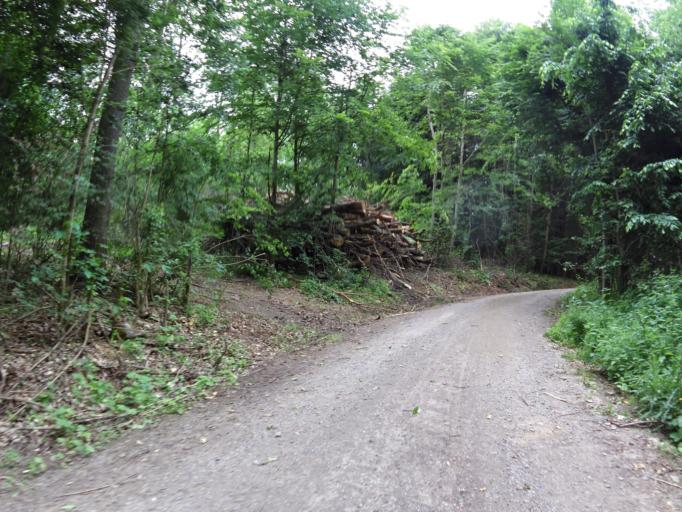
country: DE
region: Bavaria
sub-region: Regierungsbezirk Unterfranken
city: Hettstadt
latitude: 49.8160
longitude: 9.8349
